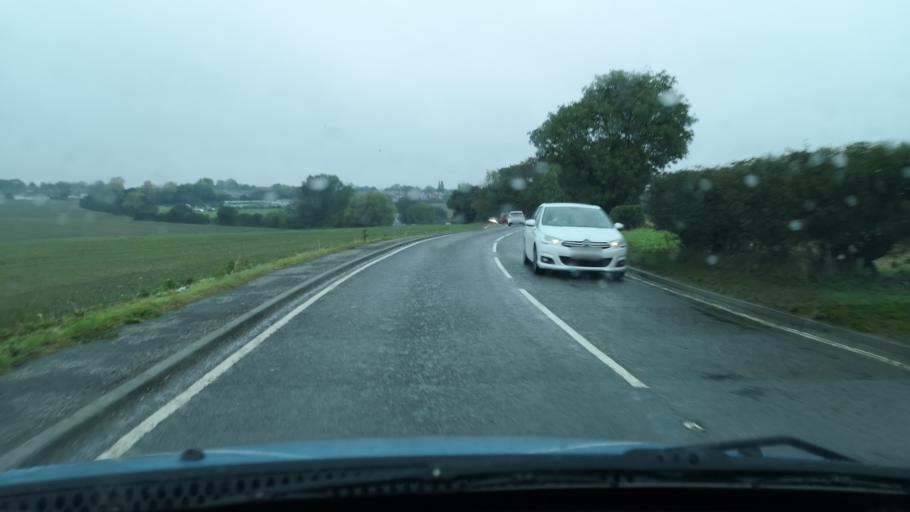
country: GB
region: England
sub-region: City and Borough of Wakefield
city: Low Ackworth
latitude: 53.6313
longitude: -1.3364
